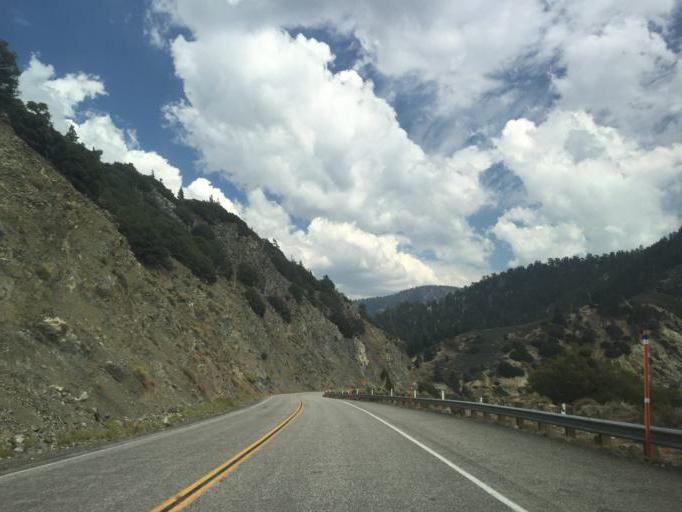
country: US
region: California
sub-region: Los Angeles County
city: Littlerock
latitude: 34.3566
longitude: -117.8565
